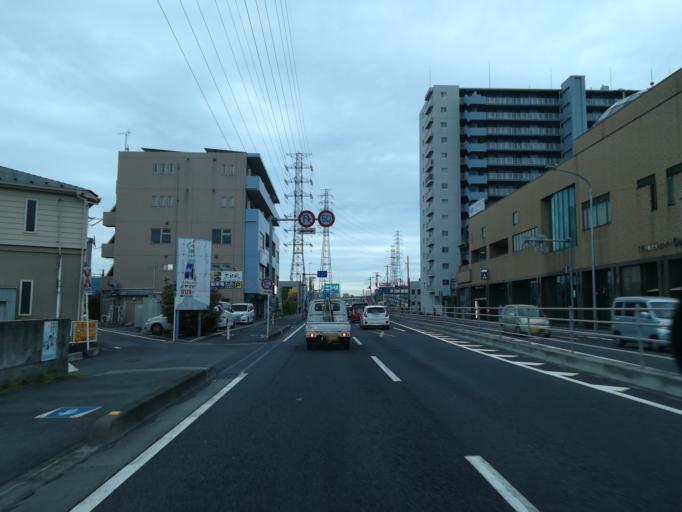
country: JP
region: Saitama
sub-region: Kawaguchi-shi
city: Hatogaya-honcho
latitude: 35.8314
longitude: 139.7359
